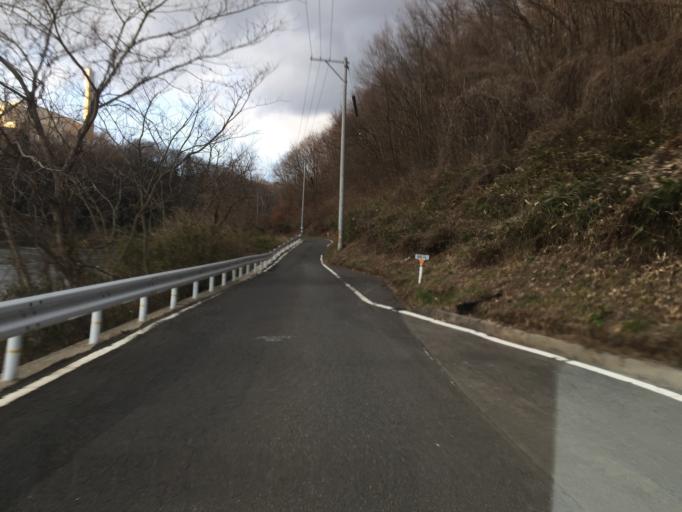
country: JP
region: Fukushima
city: Motomiya
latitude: 37.5290
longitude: 140.4153
